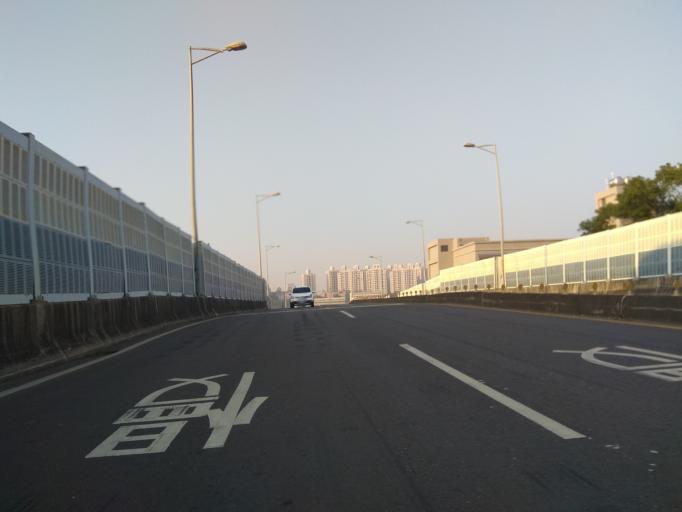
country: TW
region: Taiwan
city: Daxi
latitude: 24.9128
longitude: 121.1741
